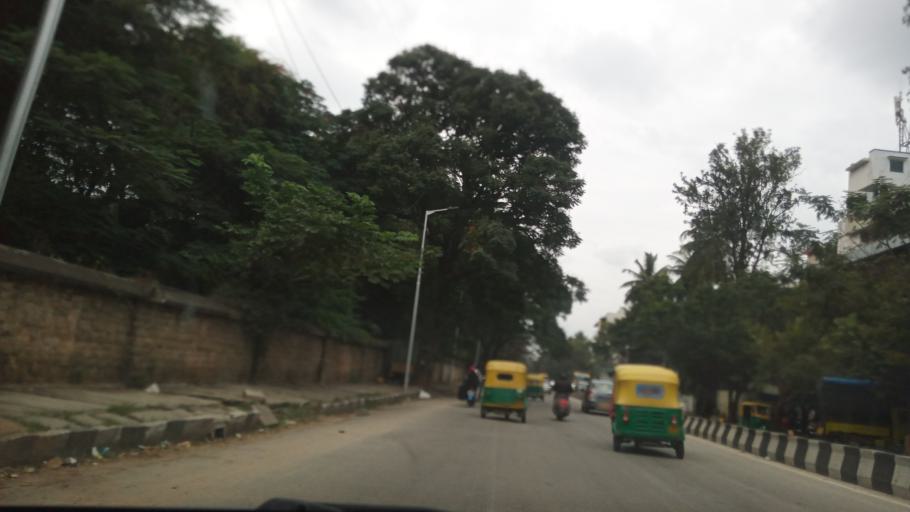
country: IN
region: Karnataka
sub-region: Bangalore Urban
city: Bangalore
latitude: 12.9981
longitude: 77.5955
